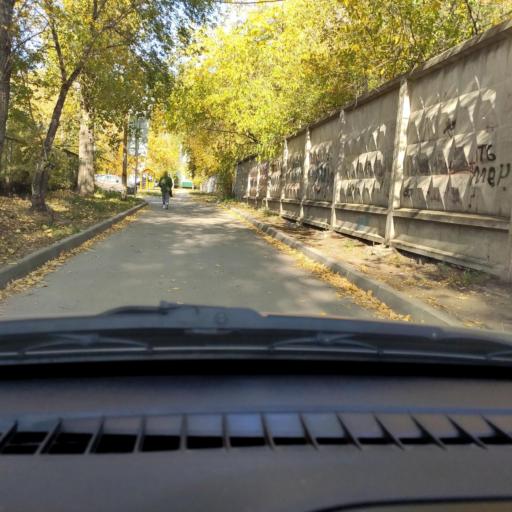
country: RU
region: Samara
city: Zhigulevsk
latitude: 53.4848
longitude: 49.4820
